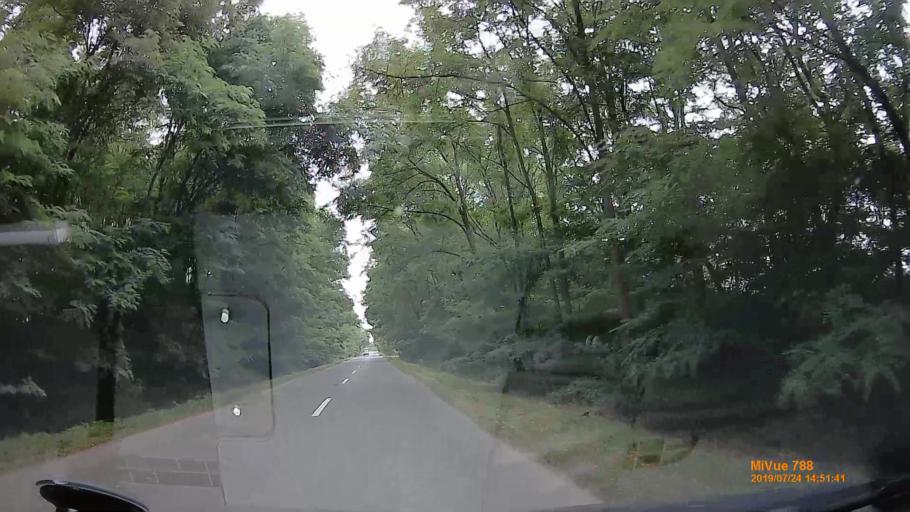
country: HU
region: Szabolcs-Szatmar-Bereg
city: Aranyosapati
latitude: 48.2700
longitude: 22.2860
